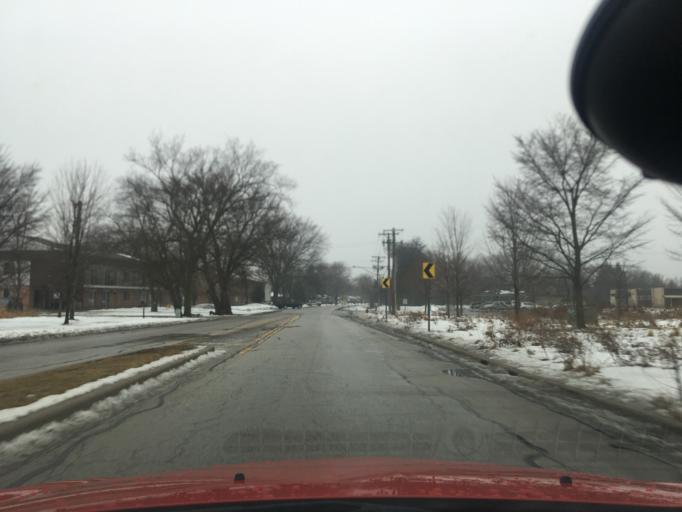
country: US
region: Illinois
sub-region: Kane County
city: North Aurora
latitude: 41.7943
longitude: -88.2684
